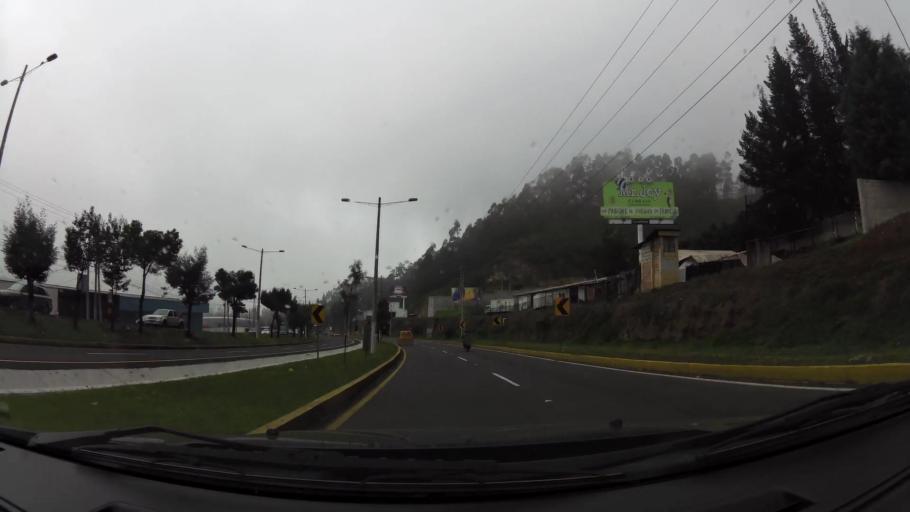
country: EC
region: Pichincha
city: Quito
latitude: -0.2606
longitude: -78.4882
